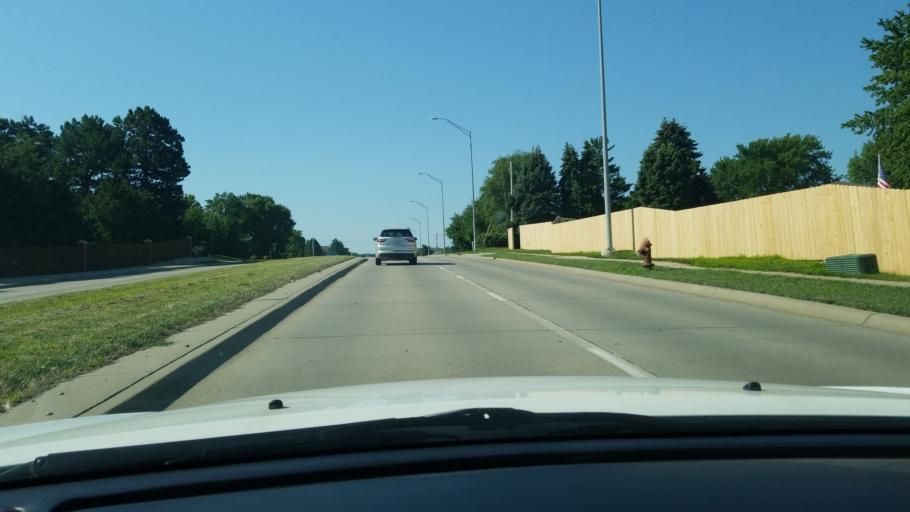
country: US
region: Nebraska
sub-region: Lancaster County
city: Lincoln
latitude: 40.7660
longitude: -96.6062
